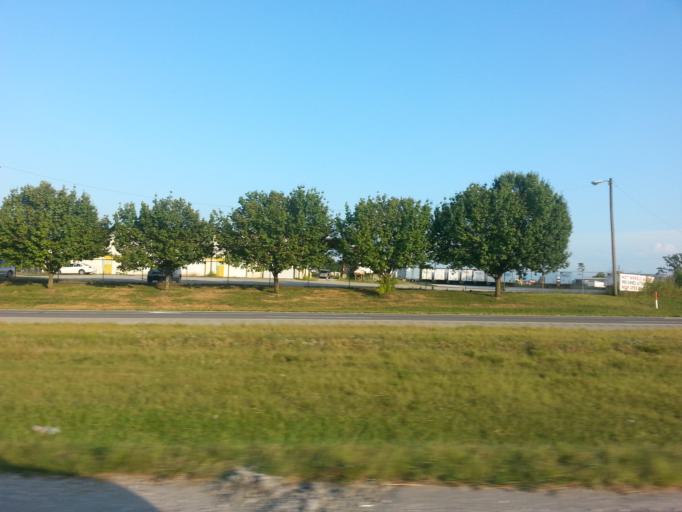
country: US
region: Tennessee
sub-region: Knox County
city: Knoxville
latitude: 36.0308
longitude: -83.8473
